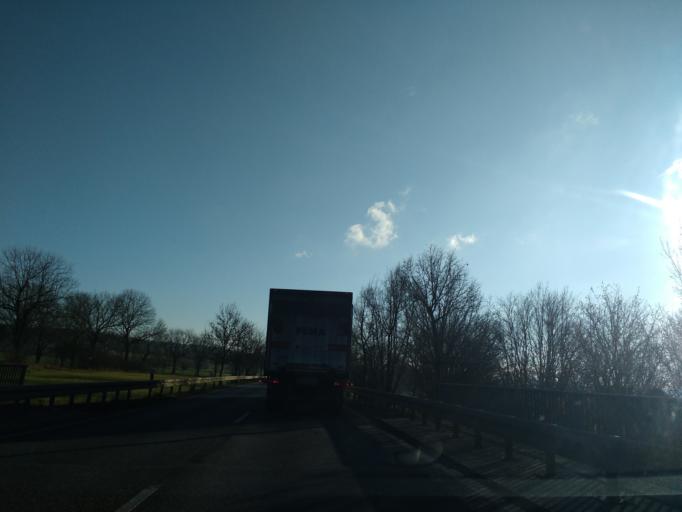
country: DE
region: Hesse
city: Schwalmstadt
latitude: 50.9077
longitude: 9.2569
